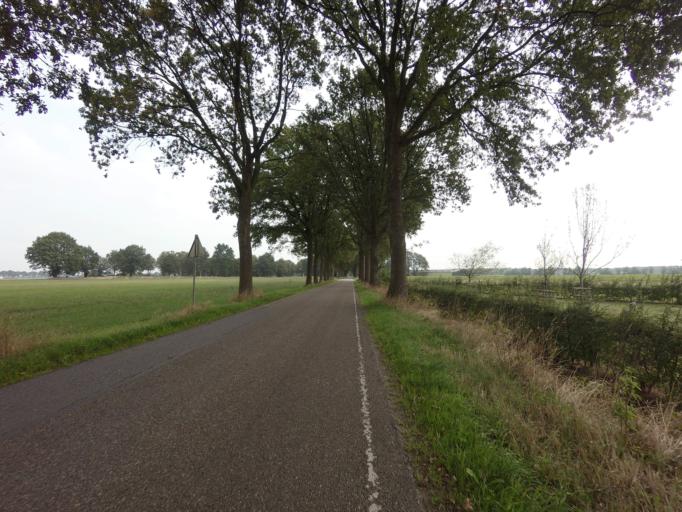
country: NL
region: Drenthe
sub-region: Gemeente Assen
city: Assen
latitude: 52.9112
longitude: 6.5222
